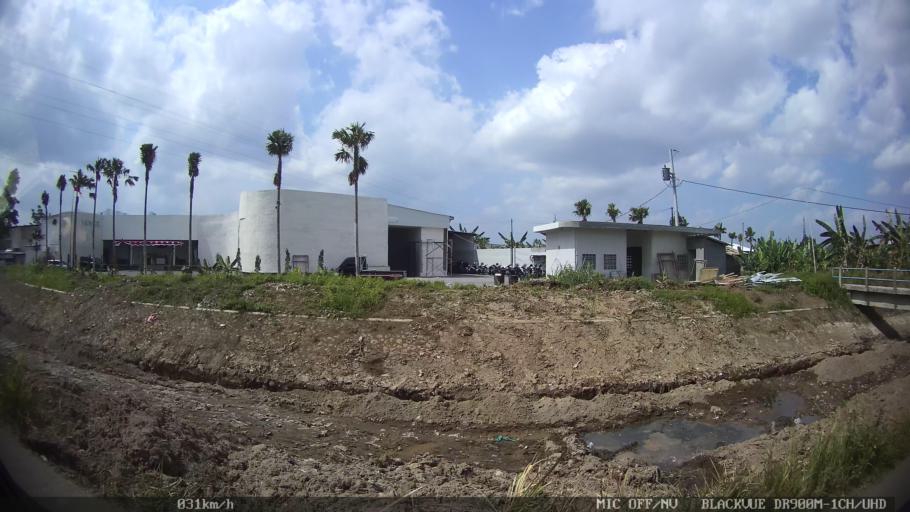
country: ID
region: Daerah Istimewa Yogyakarta
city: Yogyakarta
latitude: -7.7578
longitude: 110.3586
